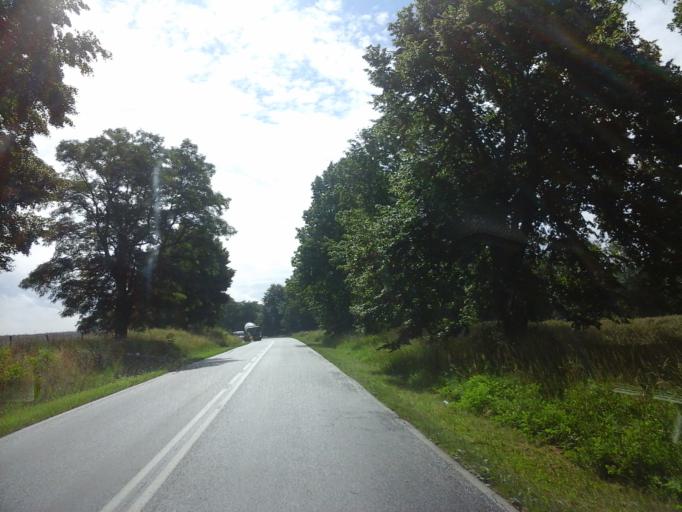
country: PL
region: West Pomeranian Voivodeship
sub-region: Powiat choszczenski
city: Choszczno
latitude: 53.1484
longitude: 15.4443
